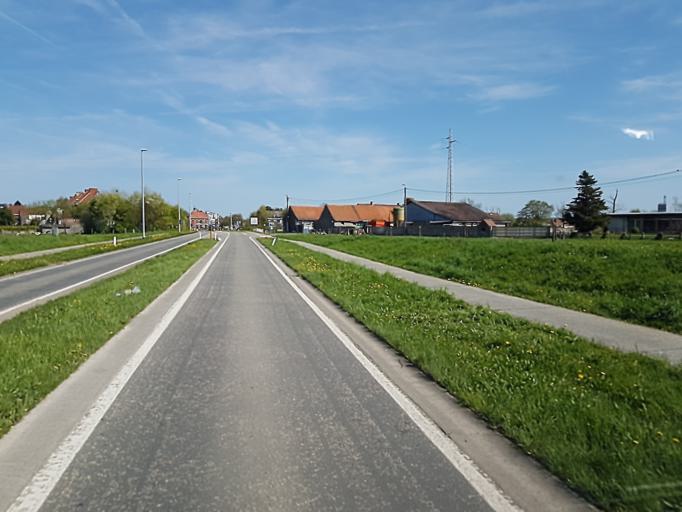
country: BE
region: Flanders
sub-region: Provincie Oost-Vlaanderen
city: Ronse
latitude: 50.7402
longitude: 3.5835
